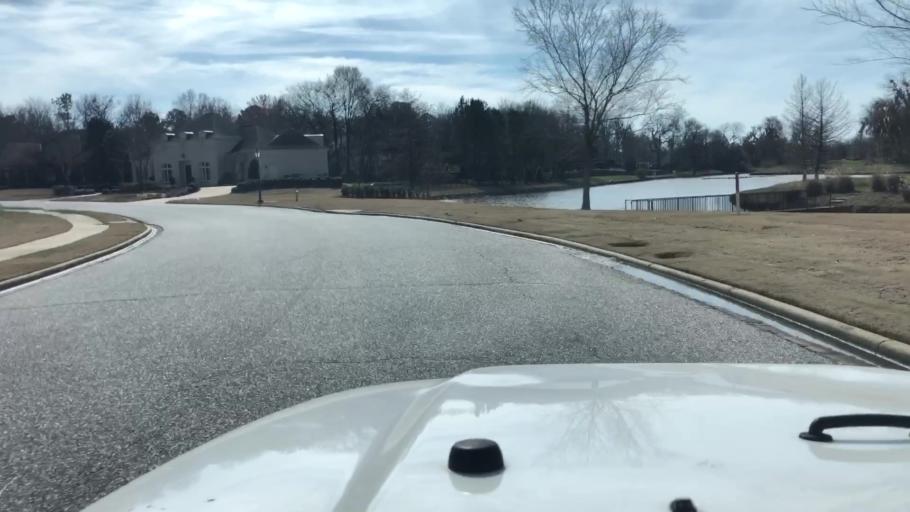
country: US
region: Alabama
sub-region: Montgomery County
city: Pike Road
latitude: 32.3492
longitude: -86.1604
